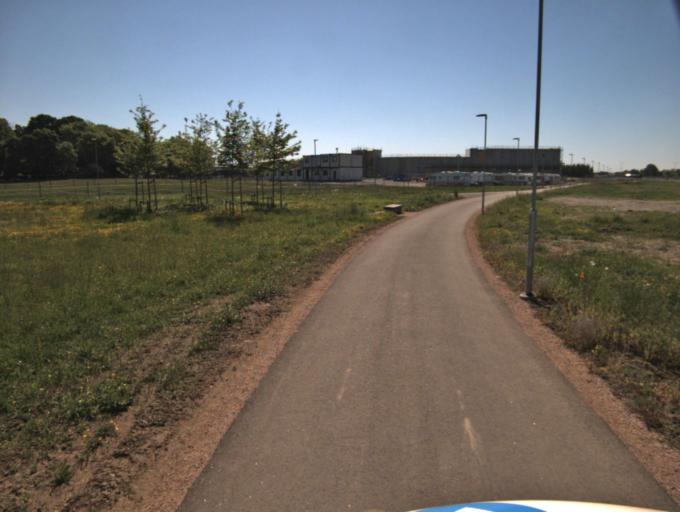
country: SE
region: Skane
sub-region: Kristianstads Kommun
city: Kristianstad
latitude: 56.0267
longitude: 14.1914
